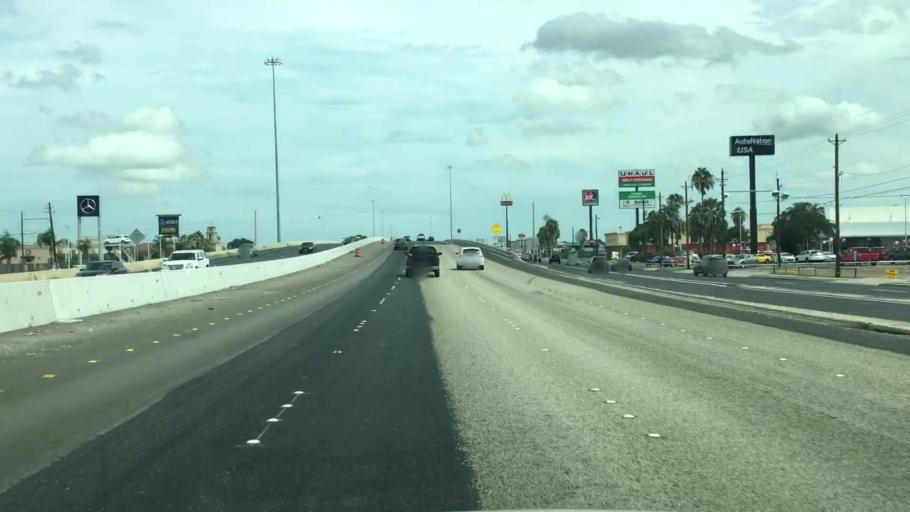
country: US
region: Texas
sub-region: Nueces County
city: Corpus Christi
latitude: 27.7299
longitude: -97.4158
